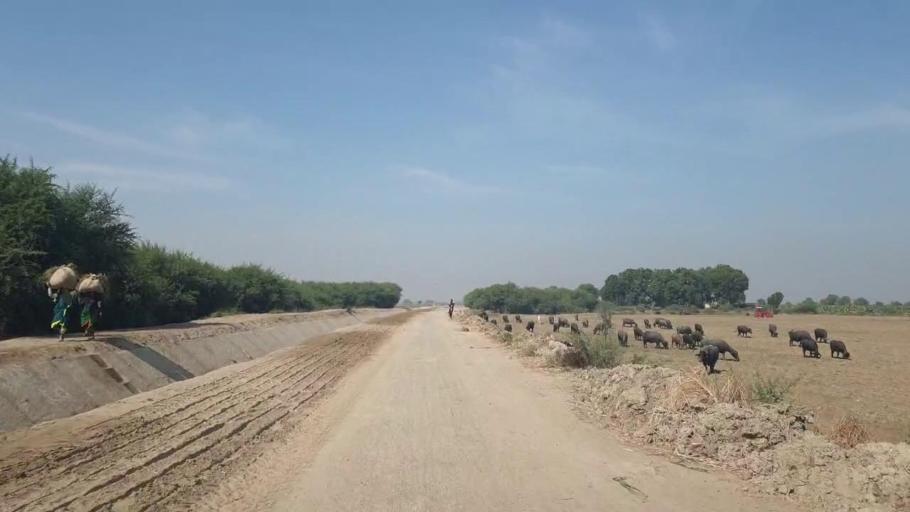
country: PK
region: Sindh
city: Matiari
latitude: 25.6824
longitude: 68.3376
